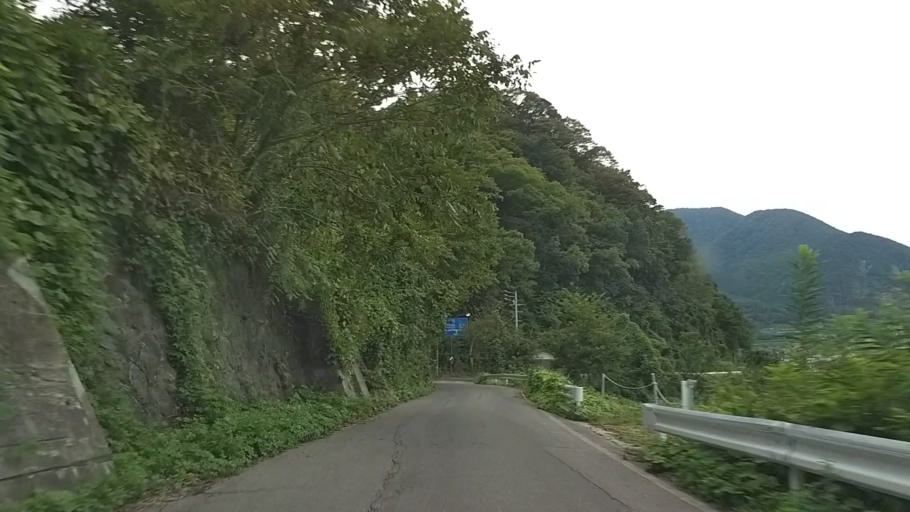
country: JP
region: Nagano
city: Iiyama
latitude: 36.8054
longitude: 138.3451
